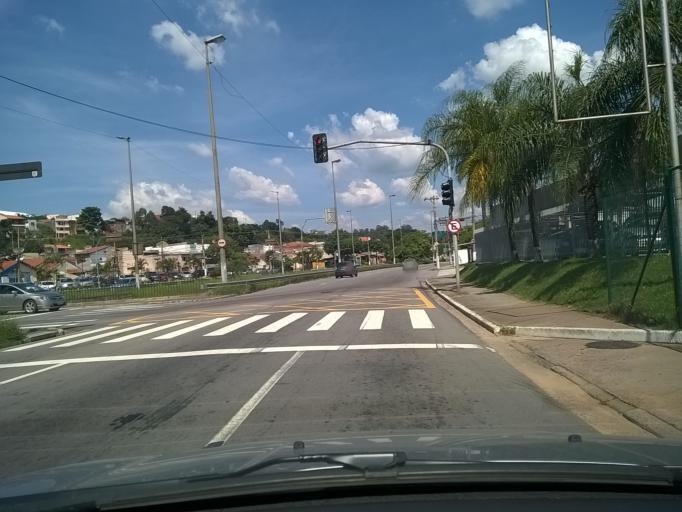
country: BR
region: Sao Paulo
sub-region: Jundiai
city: Jundiai
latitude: -23.2114
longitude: -46.8749
